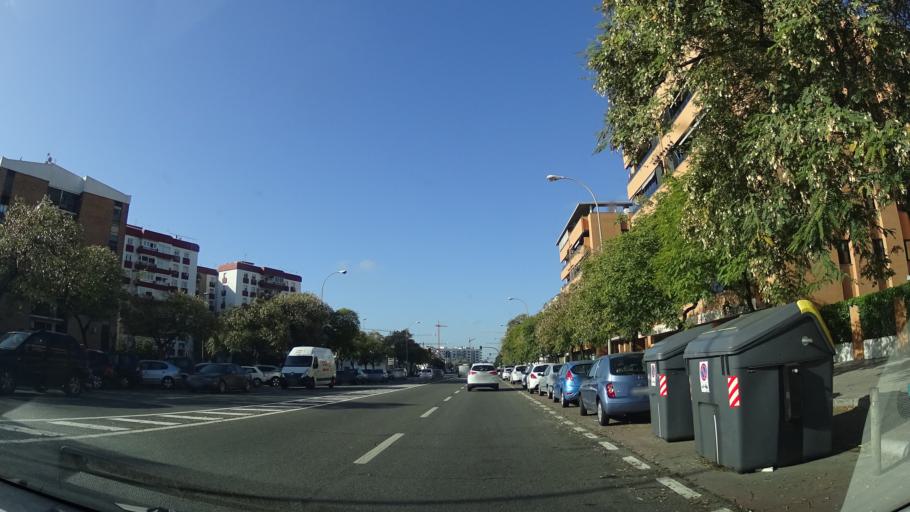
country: ES
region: Andalusia
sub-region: Province of Cordoba
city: Cordoba
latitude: 37.8837
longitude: -4.7975
